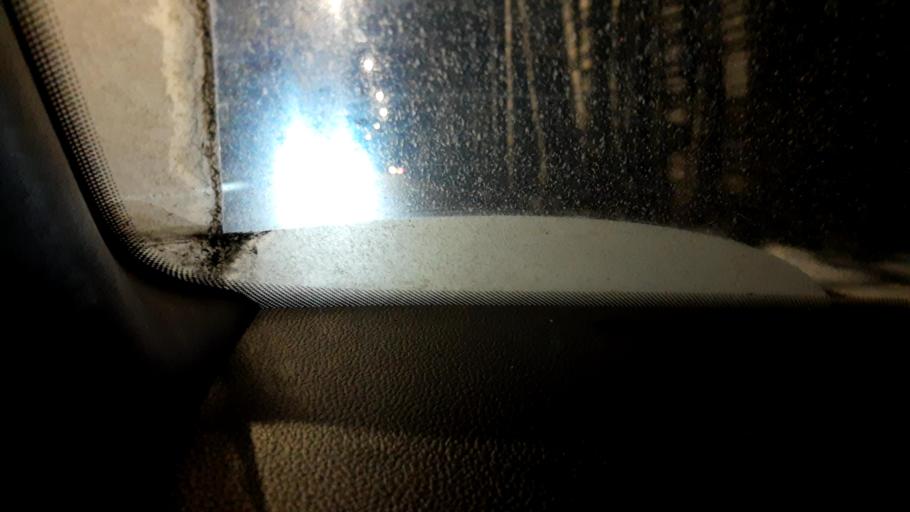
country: RU
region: Moscow
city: Annino
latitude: 55.5488
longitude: 37.6210
